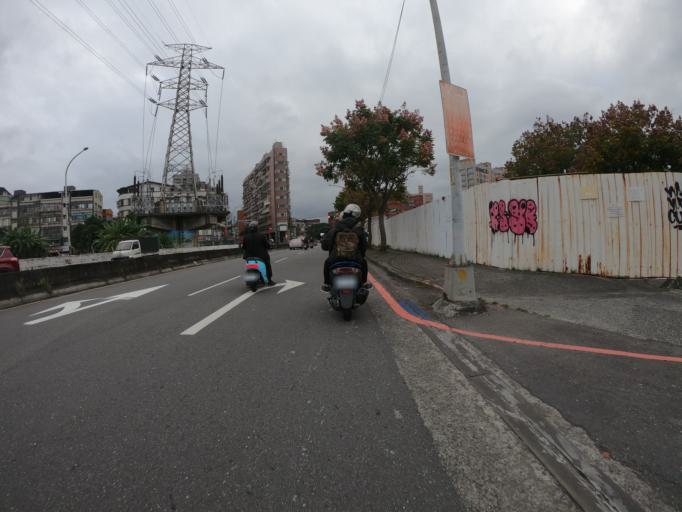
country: TW
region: Taipei
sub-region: Taipei
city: Banqiao
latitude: 25.0092
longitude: 121.4983
